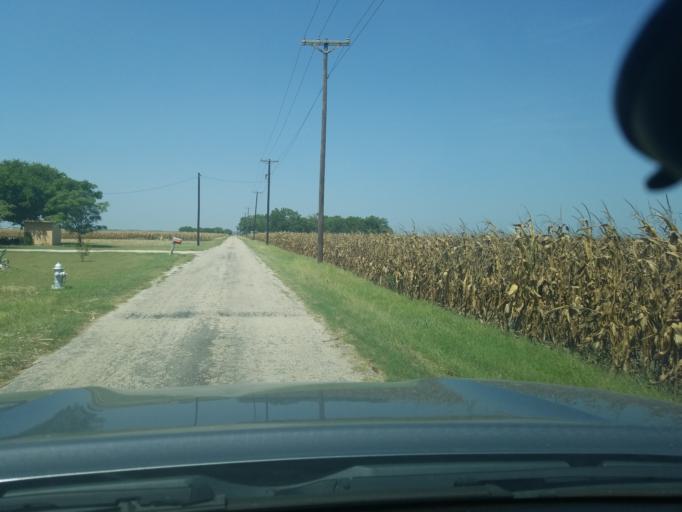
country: US
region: Texas
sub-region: Guadalupe County
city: Lake Dunlap
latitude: 29.6795
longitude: -98.0438
